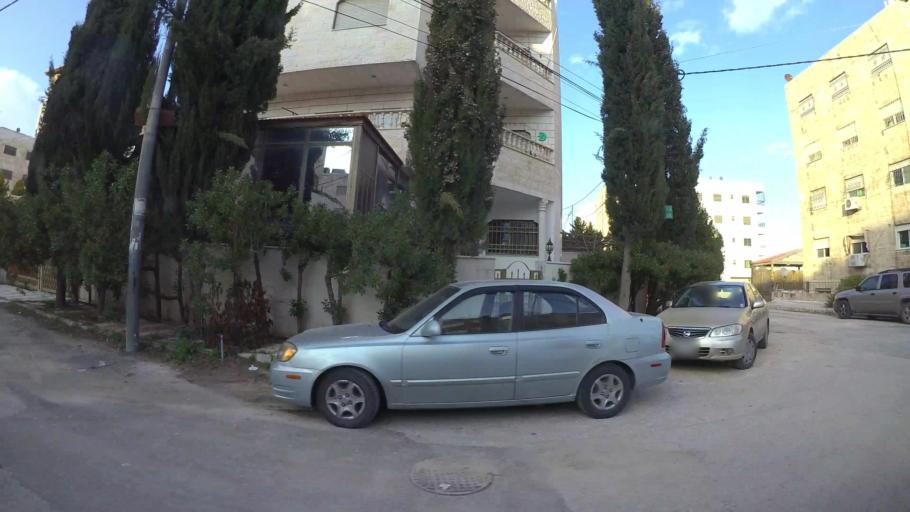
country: JO
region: Amman
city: Al Bunayyat ash Shamaliyah
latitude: 31.9121
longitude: 35.8915
